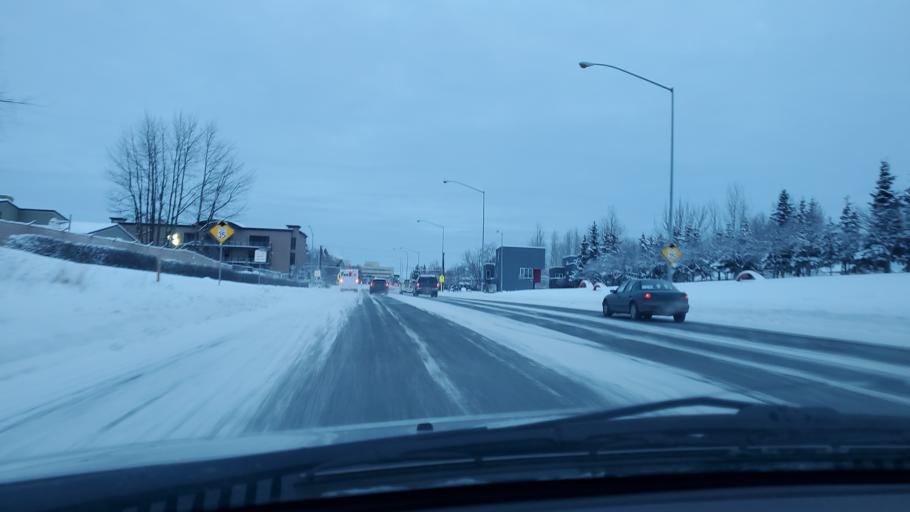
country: US
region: Alaska
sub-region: Anchorage Municipality
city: Anchorage
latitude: 61.2086
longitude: -149.8831
